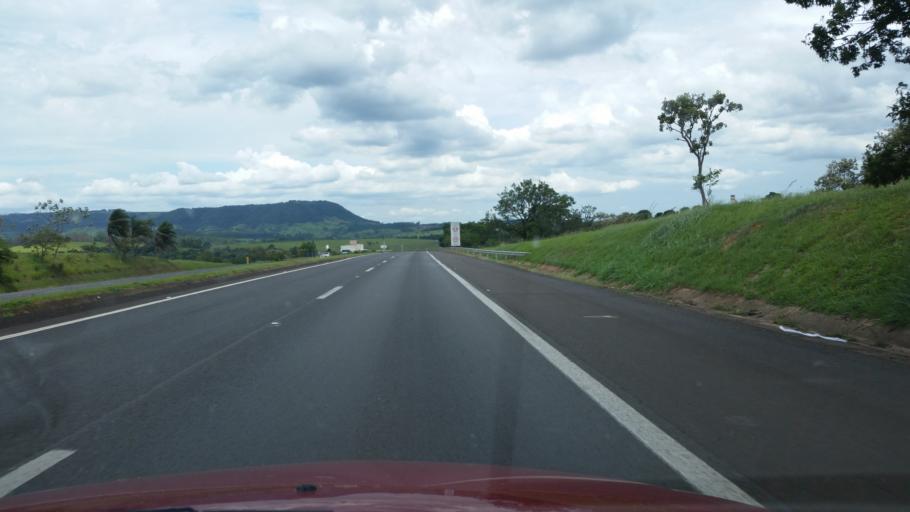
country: BR
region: Sao Paulo
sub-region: Itatinga
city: Itatinga
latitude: -23.1448
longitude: -48.4109
